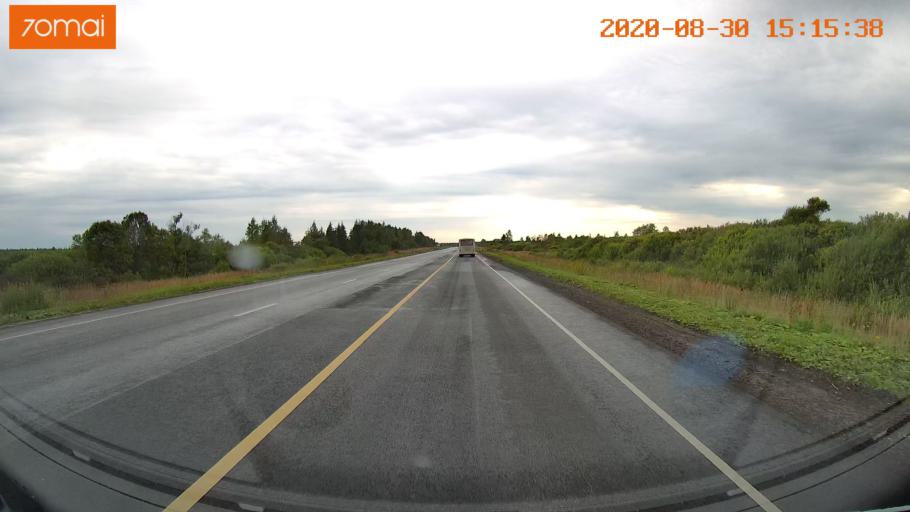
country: RU
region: Ivanovo
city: Vichuga
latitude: 57.1536
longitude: 41.8375
